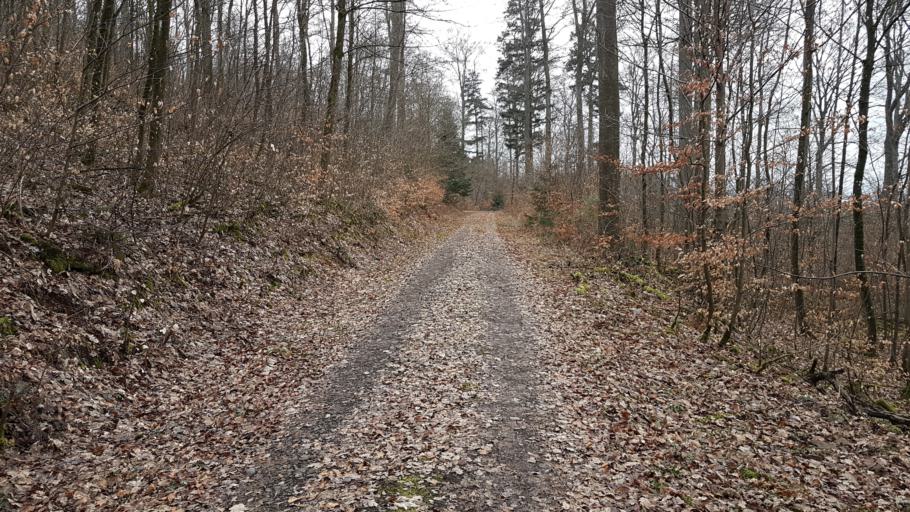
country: DE
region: Saarland
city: Sankt Wendel
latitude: 49.4410
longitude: 7.1808
